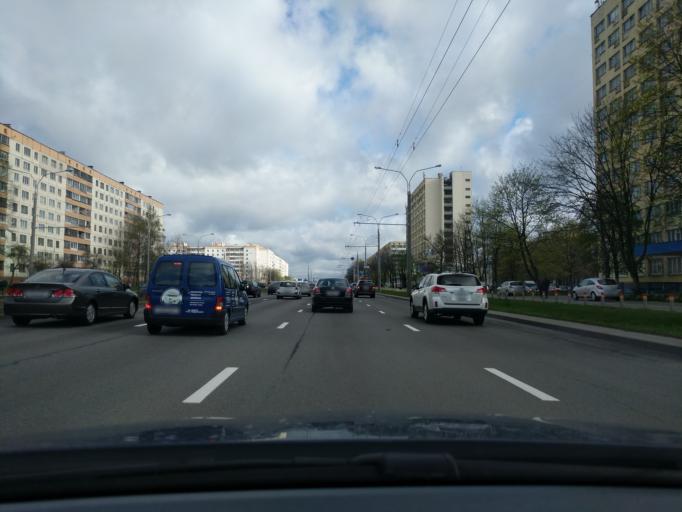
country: BY
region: Minsk
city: Novoye Medvezhino
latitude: 53.9007
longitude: 27.4970
